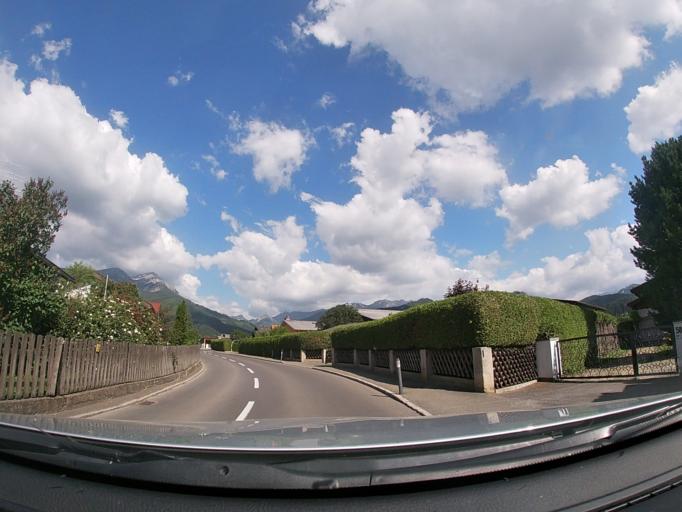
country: AT
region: Styria
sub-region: Politischer Bezirk Leoben
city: Trofaiach
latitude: 47.4256
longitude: 14.9869
